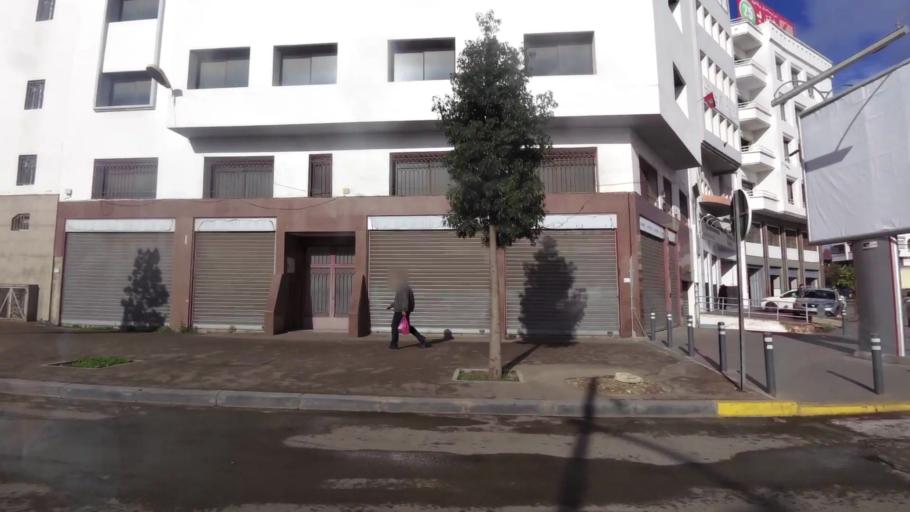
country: MA
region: Grand Casablanca
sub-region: Casablanca
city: Casablanca
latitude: 33.5535
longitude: -7.6905
